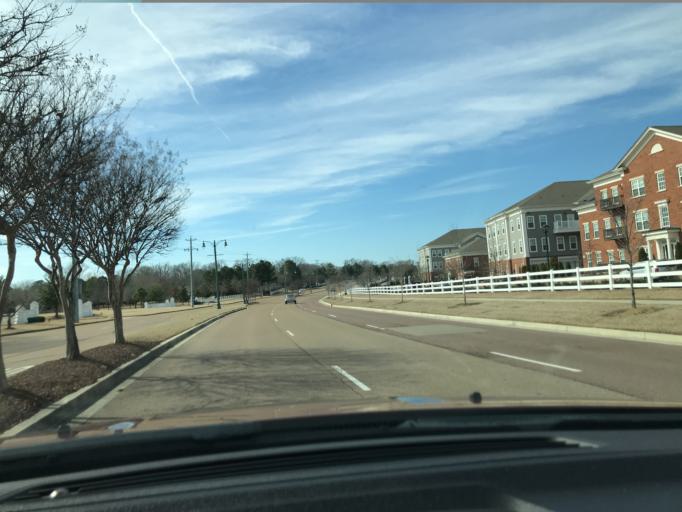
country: US
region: Tennessee
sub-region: Shelby County
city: Collierville
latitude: 35.0380
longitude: -89.7047
